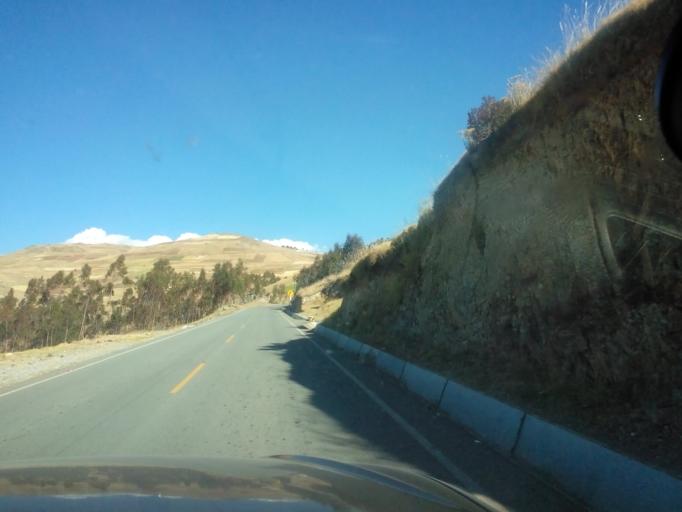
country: PE
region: Apurimac
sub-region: Provincia de Andahuaylas
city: Pacucha
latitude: -13.6556
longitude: -73.2901
